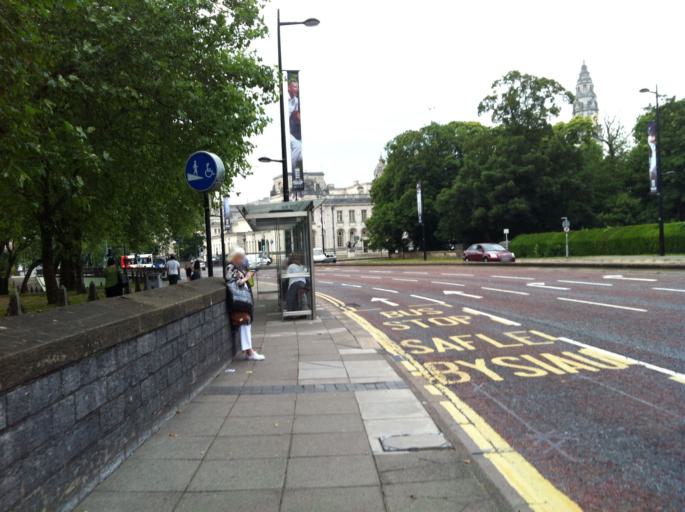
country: GB
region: Wales
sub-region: Cardiff
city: Cardiff
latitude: 51.4830
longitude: -3.1796
